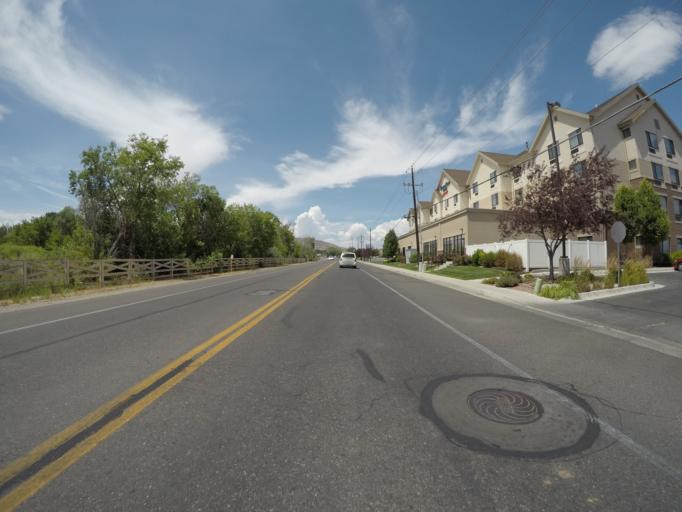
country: US
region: Utah
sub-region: Uintah County
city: Vernal
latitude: 40.4482
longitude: -109.5502
